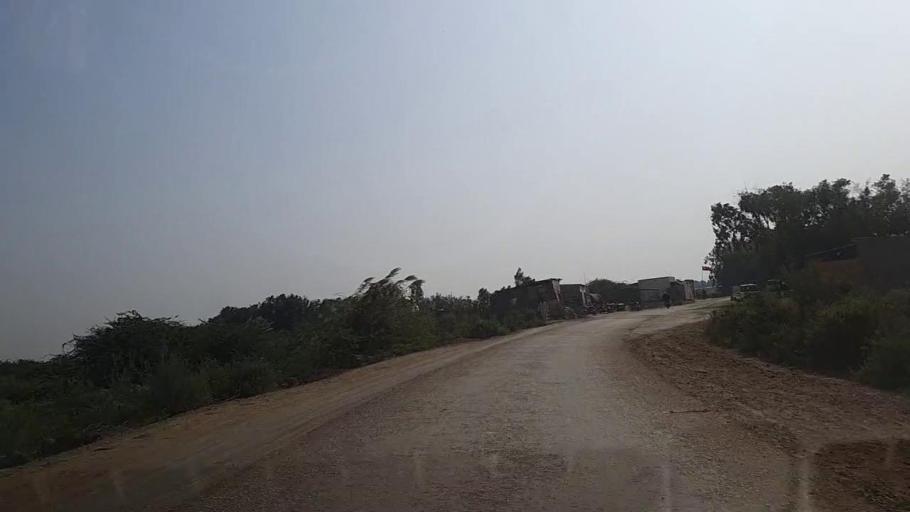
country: PK
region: Sindh
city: Keti Bandar
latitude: 24.2248
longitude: 67.6663
